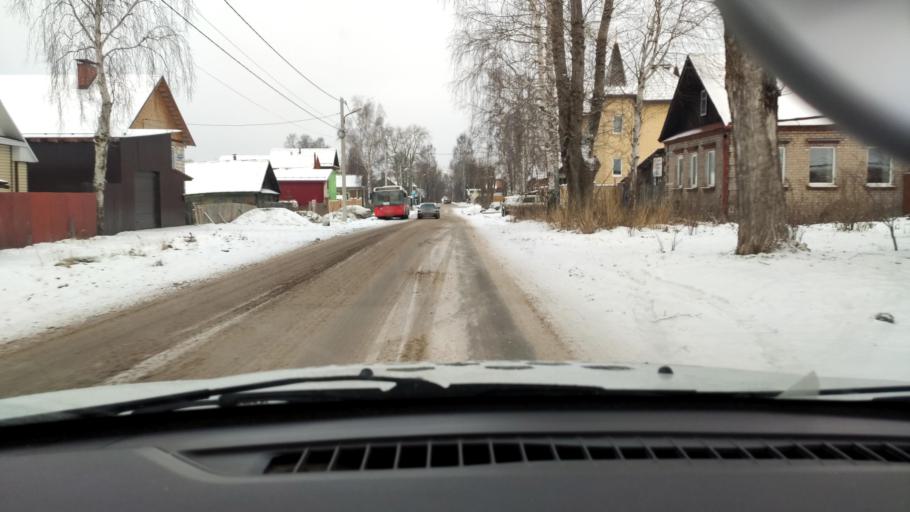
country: RU
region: Perm
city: Polazna
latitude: 58.1225
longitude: 56.3960
